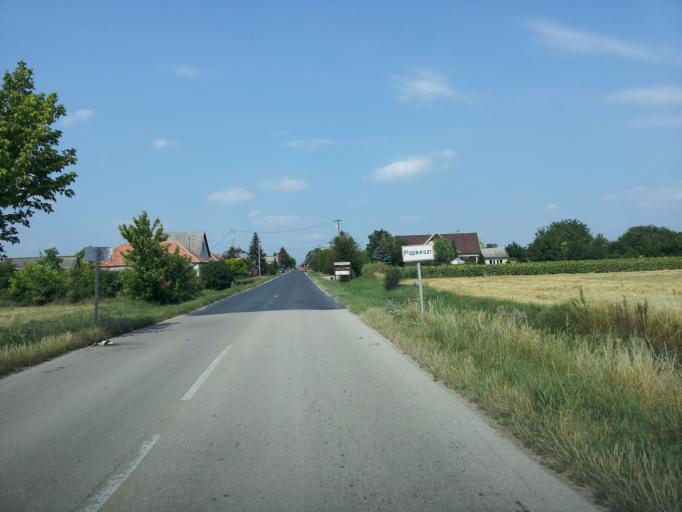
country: HU
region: Veszprem
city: Balatonkenese
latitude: 47.0756
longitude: 18.0737
